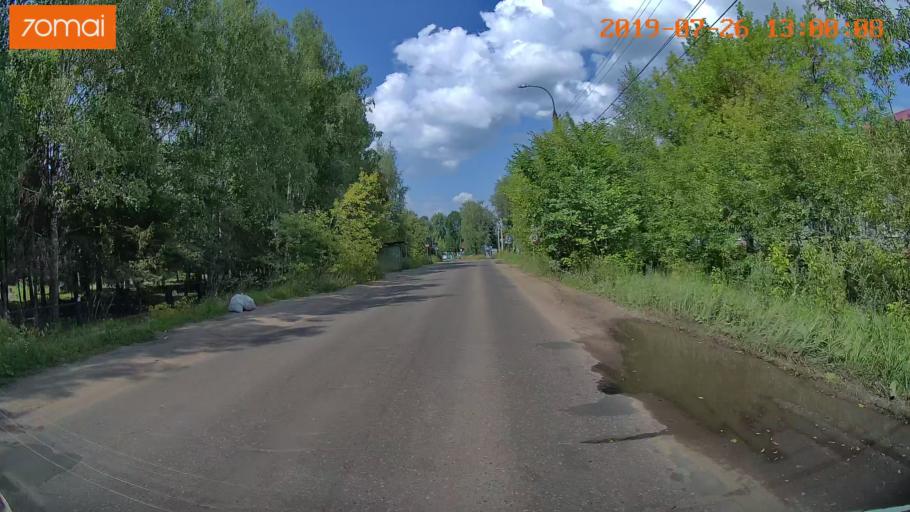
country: RU
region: Ivanovo
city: Bogorodskoye
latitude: 57.0323
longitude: 41.0178
